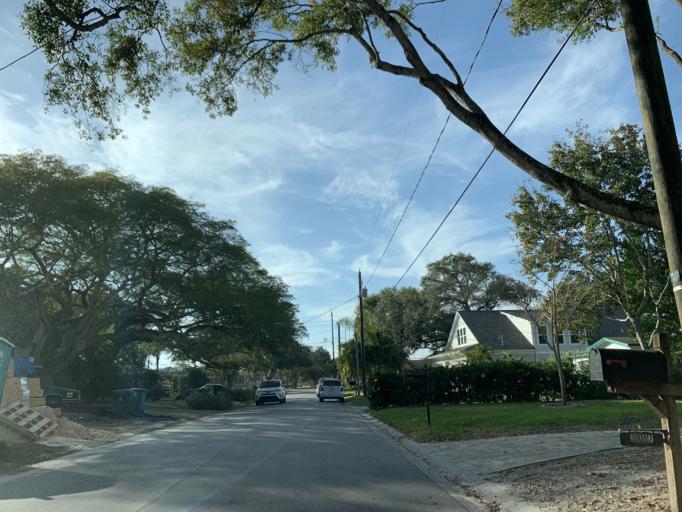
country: US
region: Florida
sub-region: Hillsborough County
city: Tampa
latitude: 27.8985
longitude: -82.5008
